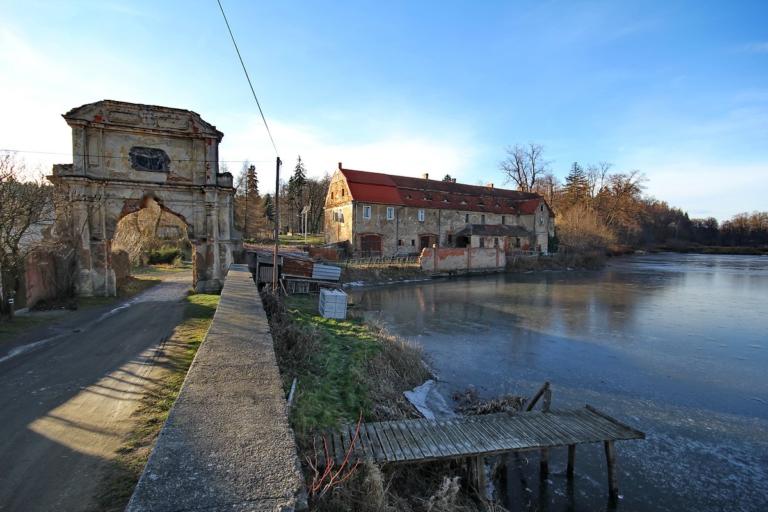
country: PL
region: Lower Silesian Voivodeship
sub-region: Powiat dzierzoniowski
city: Ostroszowice
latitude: 50.6491
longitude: 16.6878
